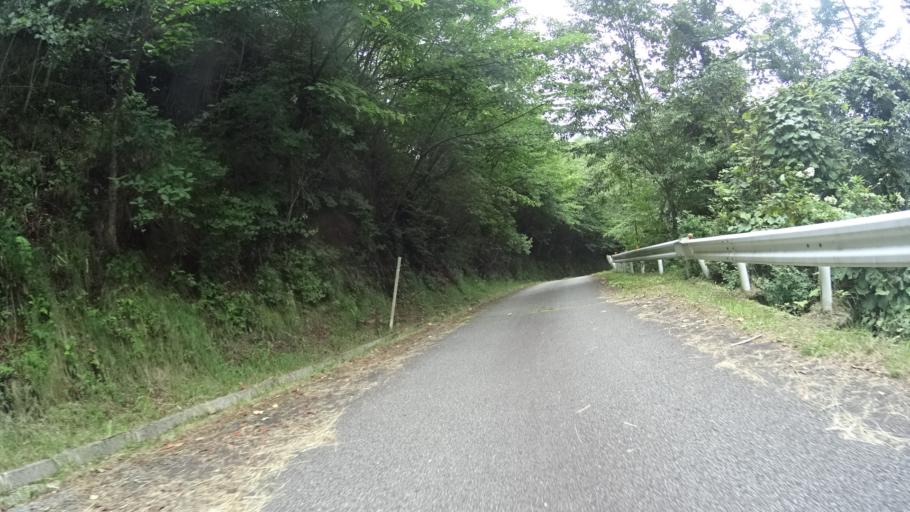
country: JP
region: Yamanashi
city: Kofu-shi
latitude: 35.8277
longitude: 138.5798
